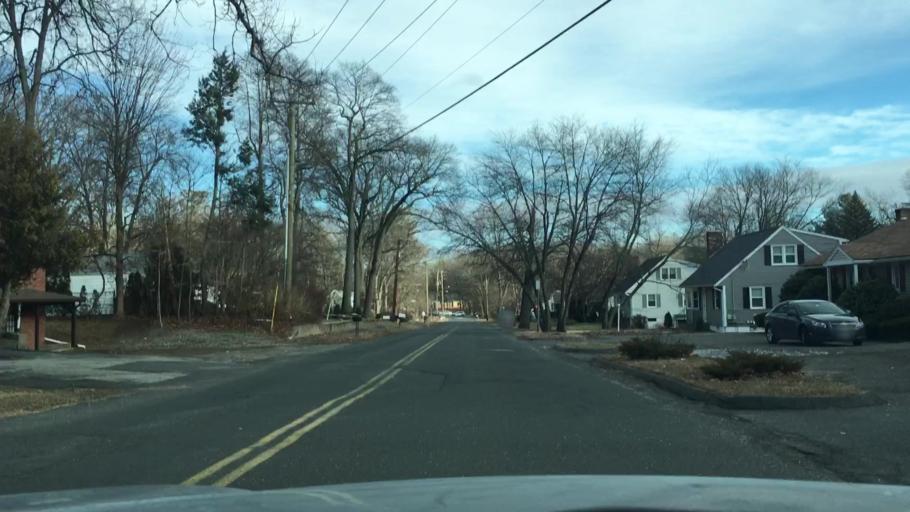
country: US
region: Massachusetts
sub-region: Hampden County
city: Agawam
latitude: 42.0672
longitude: -72.6312
